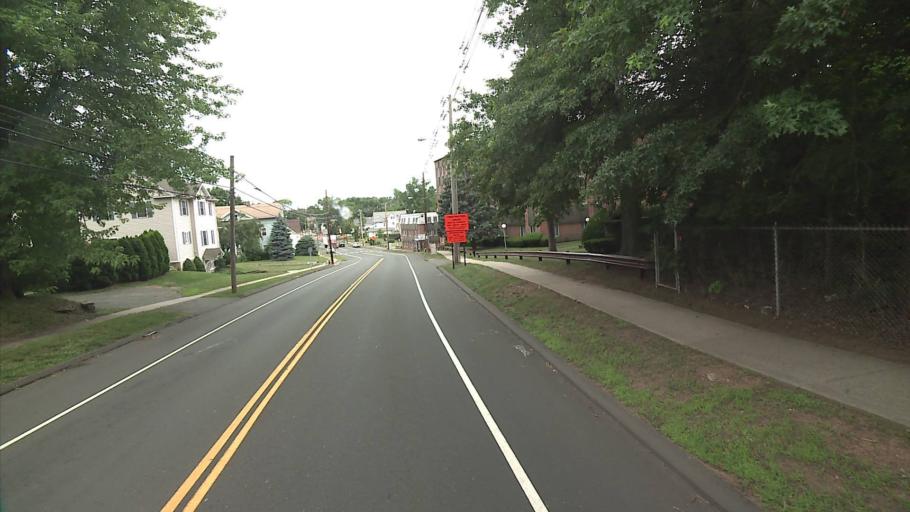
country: US
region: Connecticut
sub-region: New Haven County
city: Wallingford Center
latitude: 41.4504
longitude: -72.8104
